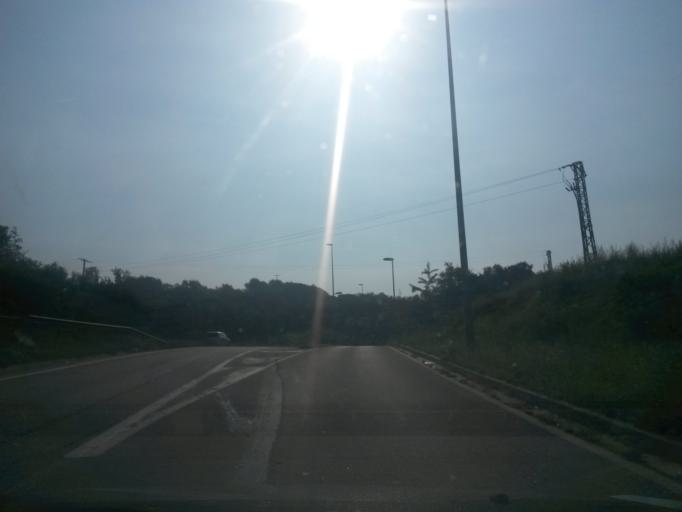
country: ES
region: Catalonia
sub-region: Provincia de Girona
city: Fornells de la Selva
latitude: 41.9557
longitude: 2.8110
